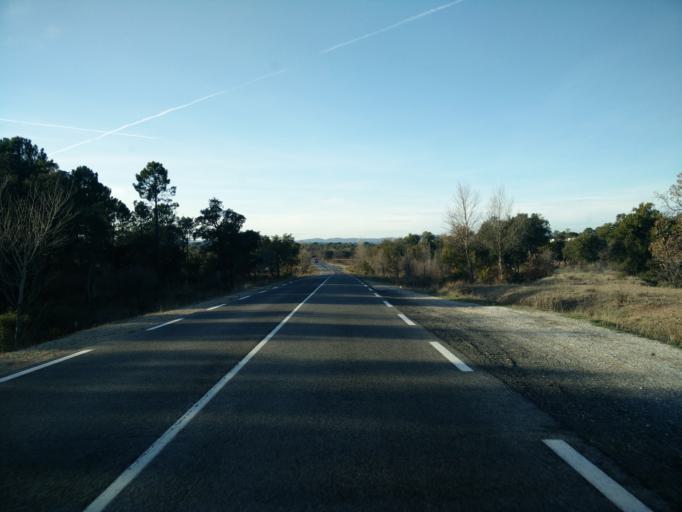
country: FR
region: Provence-Alpes-Cote d'Azur
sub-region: Departement du Var
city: La Garde-Freinet
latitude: 43.3526
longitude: 6.4189
